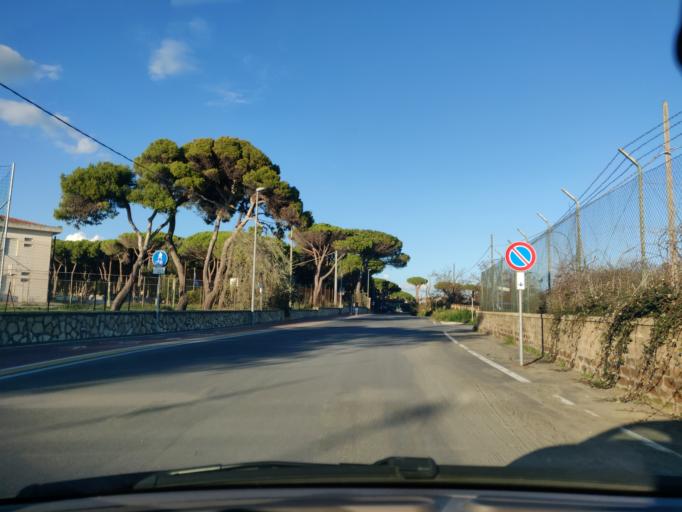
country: IT
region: Latium
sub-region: Provincia di Viterbo
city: Tarquinia
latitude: 42.2145
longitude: 11.7092
